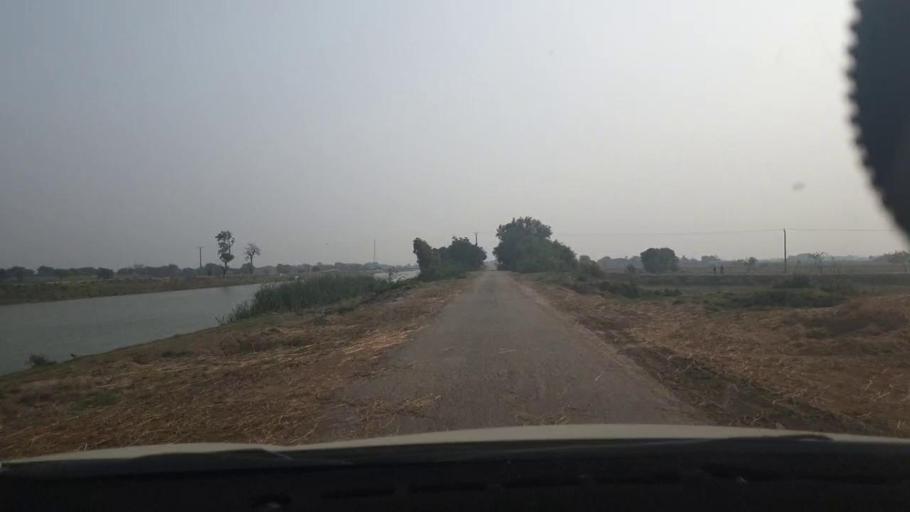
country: PK
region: Sindh
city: Tando Muhammad Khan
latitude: 24.9703
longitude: 68.4940
